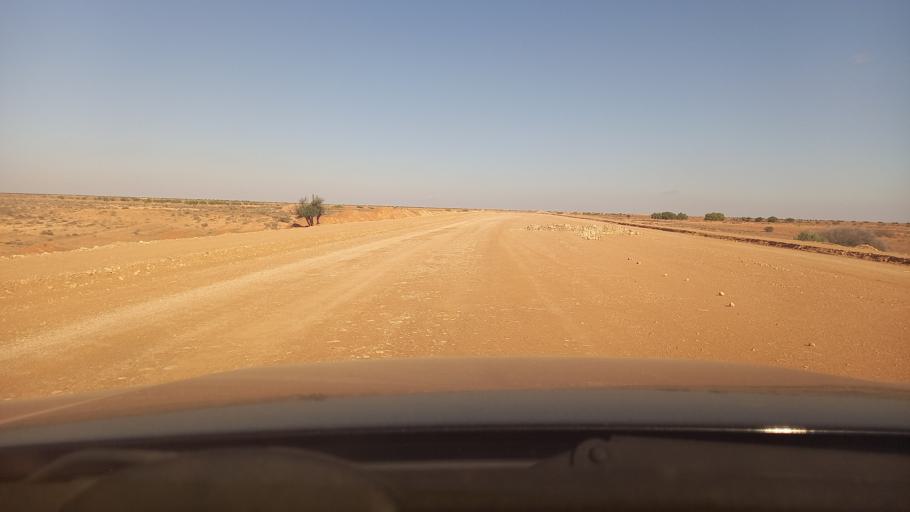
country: TN
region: Madanin
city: Medenine
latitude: 33.1389
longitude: 10.5053
